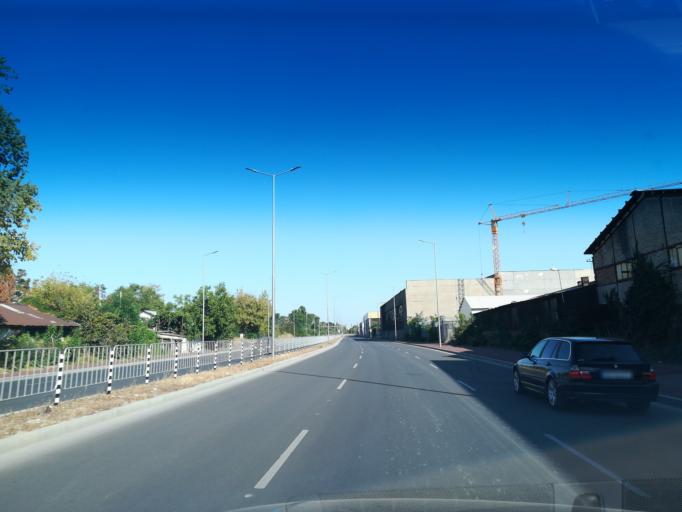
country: BG
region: Plovdiv
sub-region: Obshtina Plovdiv
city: Plovdiv
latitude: 42.1656
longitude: 24.7553
